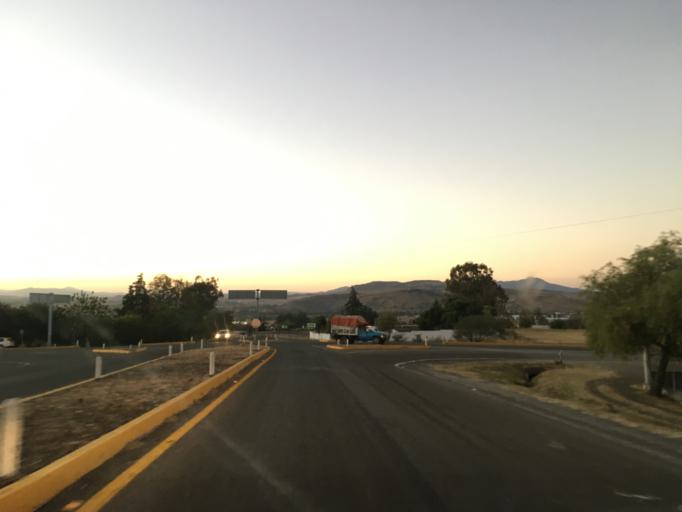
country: MX
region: Michoacan
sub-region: Zinapecuaro
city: Santa Clara del Tule
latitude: 19.8207
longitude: -100.8233
